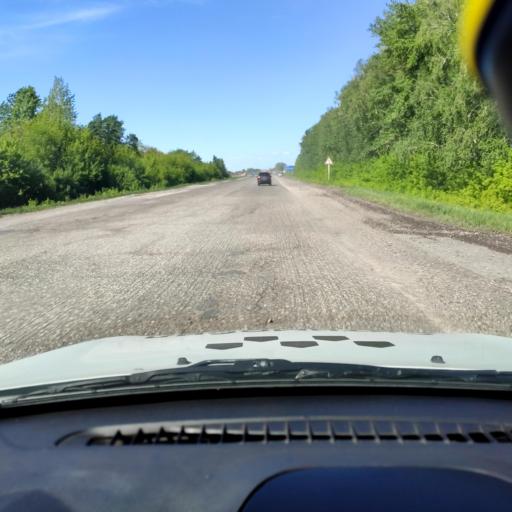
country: RU
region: Samara
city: Tol'yatti
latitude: 53.6544
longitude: 49.4241
